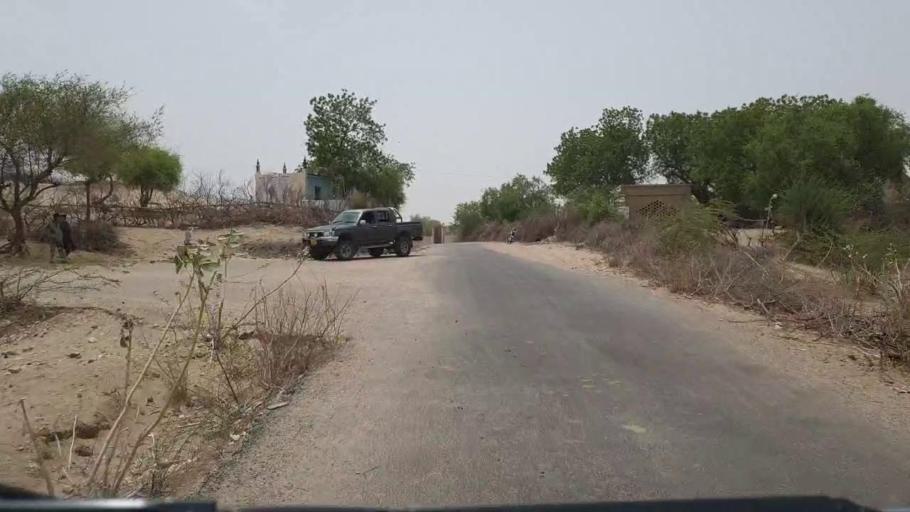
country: PK
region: Sindh
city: Naukot
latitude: 24.7839
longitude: 69.5316
